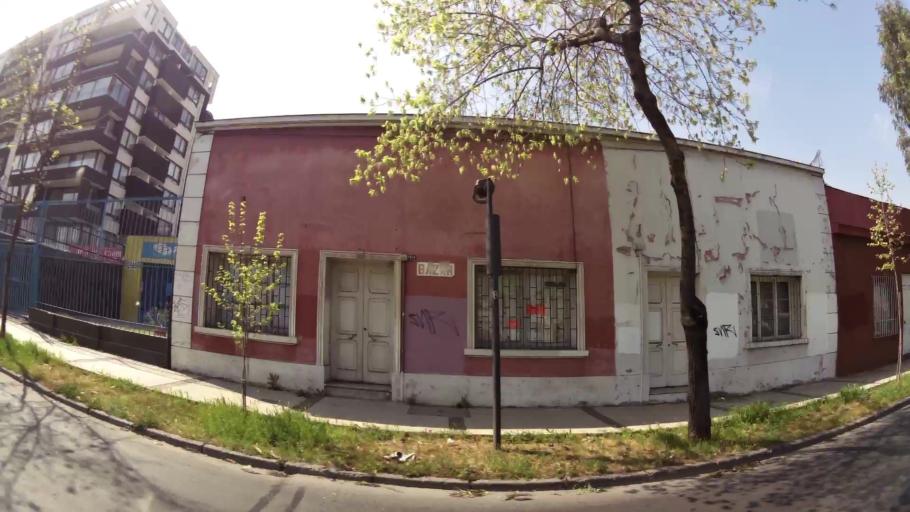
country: CL
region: Santiago Metropolitan
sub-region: Provincia de Santiago
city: Villa Presidente Frei, Nunoa, Santiago, Chile
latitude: -33.4429
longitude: -70.5994
